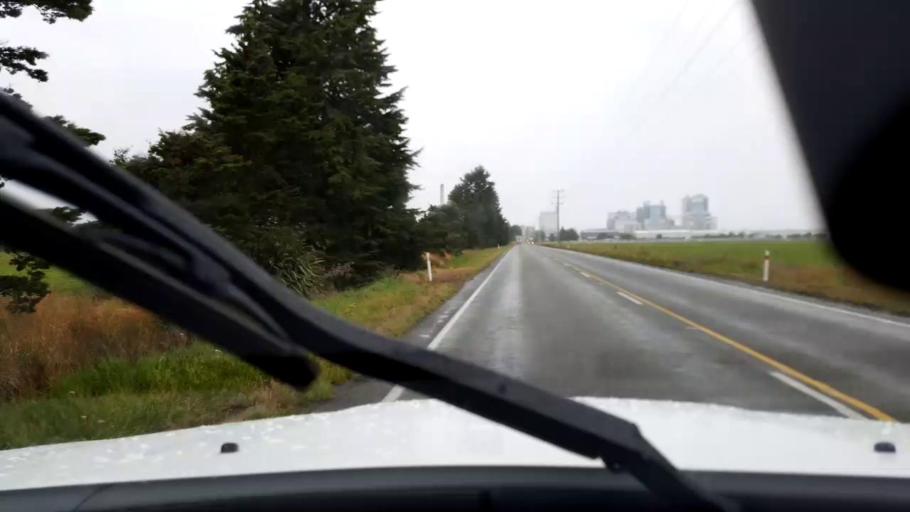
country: NZ
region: Canterbury
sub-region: Timaru District
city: Timaru
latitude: -44.2054
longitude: 171.3754
